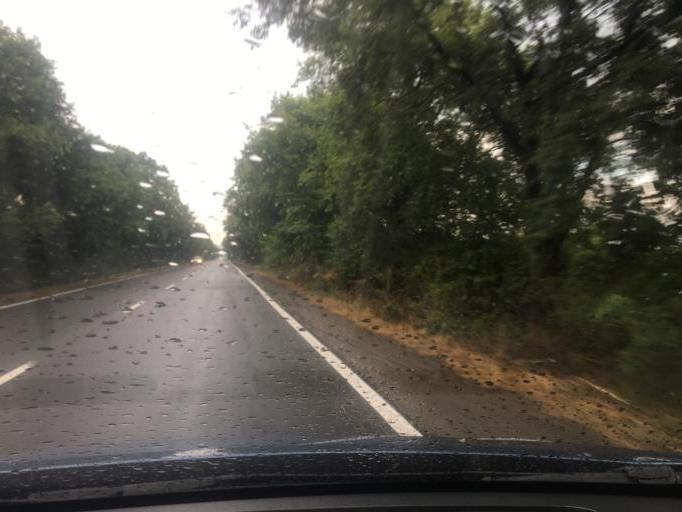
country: BG
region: Burgas
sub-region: Obshtina Pomorie
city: Pomorie
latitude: 42.5824
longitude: 27.6072
